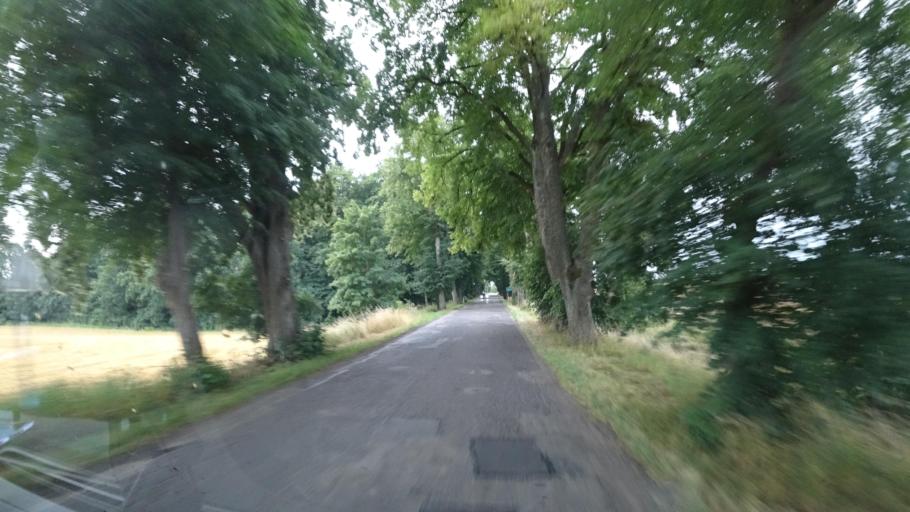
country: PL
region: Warmian-Masurian Voivodeship
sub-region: Powiat gizycki
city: Ryn
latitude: 53.9264
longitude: 21.5513
